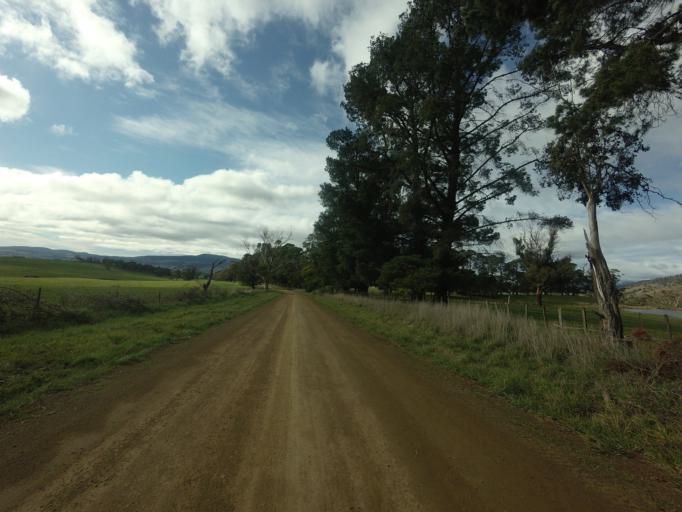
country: AU
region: Tasmania
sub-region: Derwent Valley
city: New Norfolk
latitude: -42.7175
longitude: 146.8774
